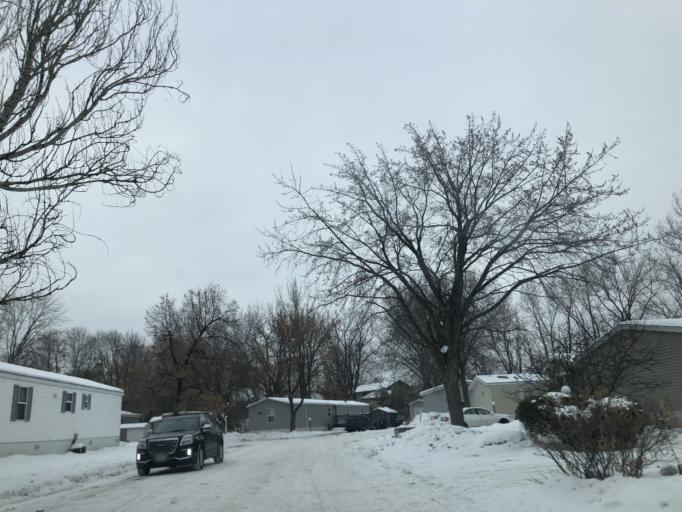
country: US
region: Minnesota
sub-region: Ramsey County
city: New Brighton
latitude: 45.0801
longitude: -93.1796
